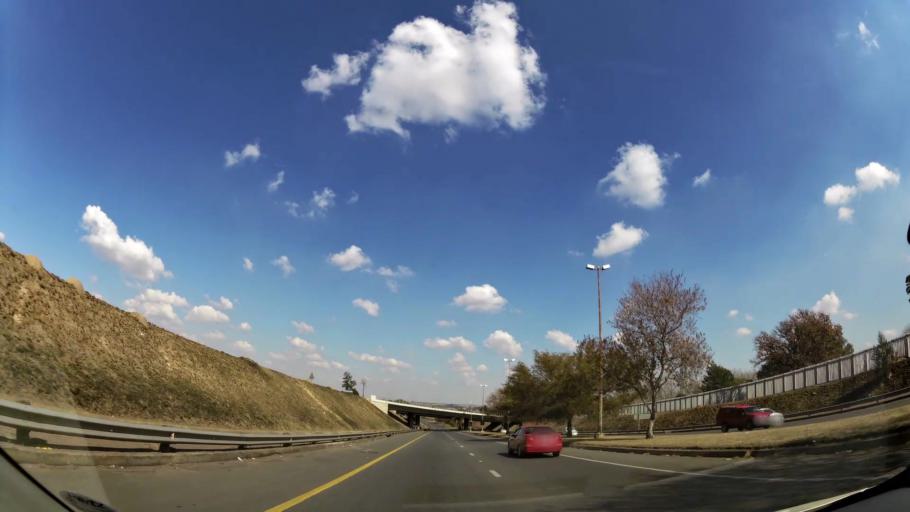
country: ZA
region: Mpumalanga
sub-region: Nkangala District Municipality
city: Witbank
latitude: -25.9154
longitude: 29.2347
